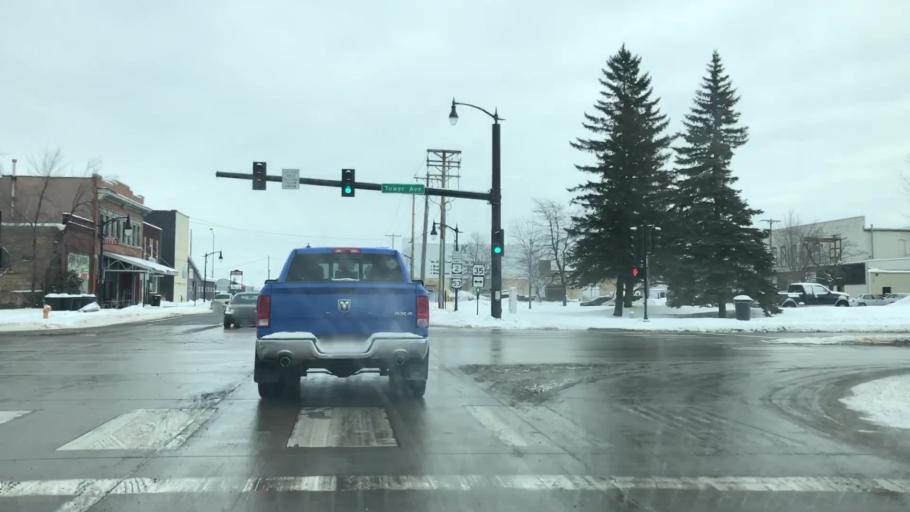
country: US
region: Wisconsin
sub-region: Douglas County
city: Superior
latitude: 46.7279
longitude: -92.1041
